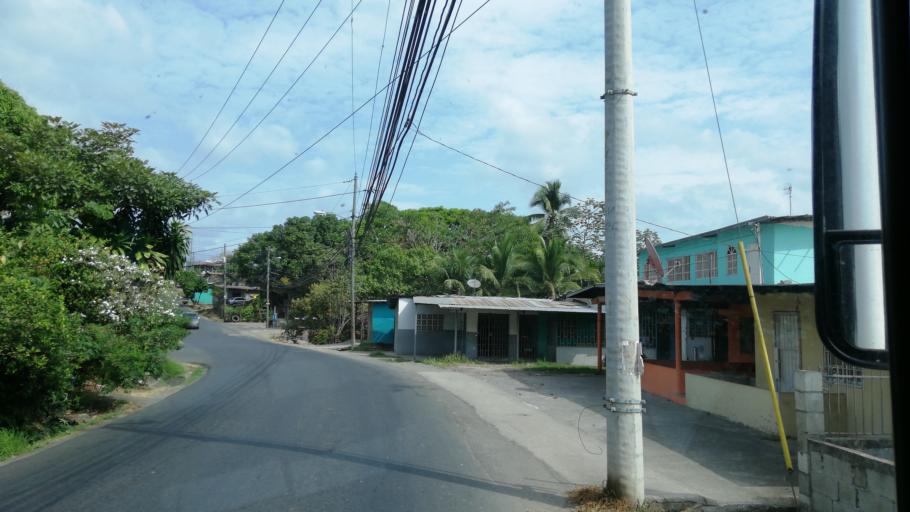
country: PA
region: Panama
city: Tocumen
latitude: 9.0995
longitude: -79.3702
